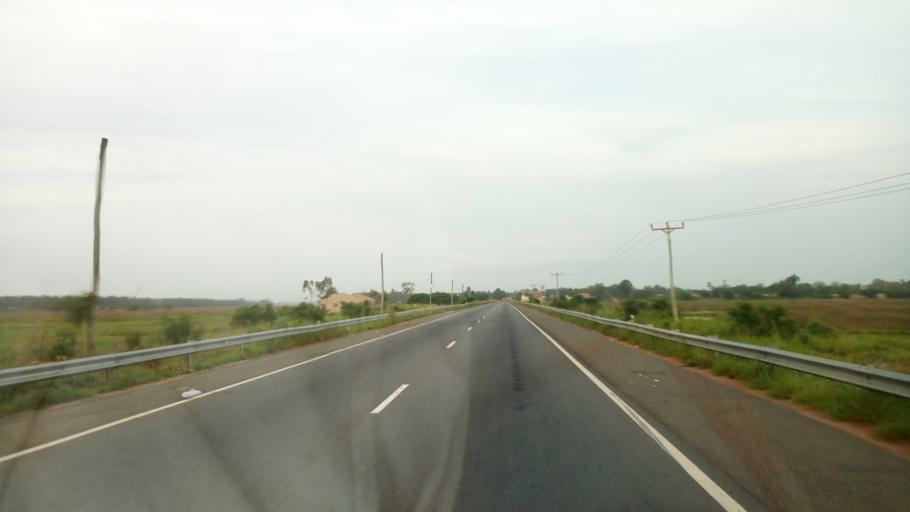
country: TG
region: Maritime
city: Lome
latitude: 6.1072
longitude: 1.1086
